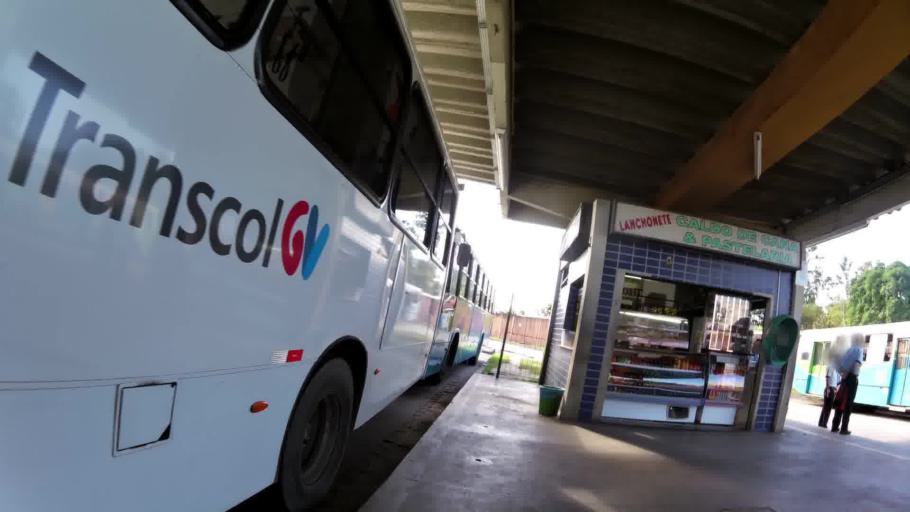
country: BR
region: Espirito Santo
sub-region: Vila Velha
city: Vila Velha
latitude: -20.2303
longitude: -40.2699
